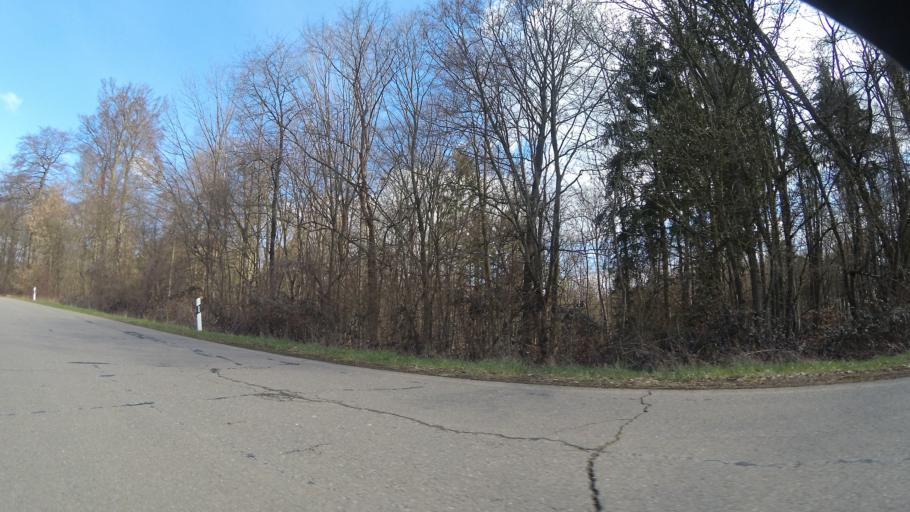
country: DE
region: Saarland
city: Rehlingen-Siersburg
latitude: 49.3908
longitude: 6.6598
